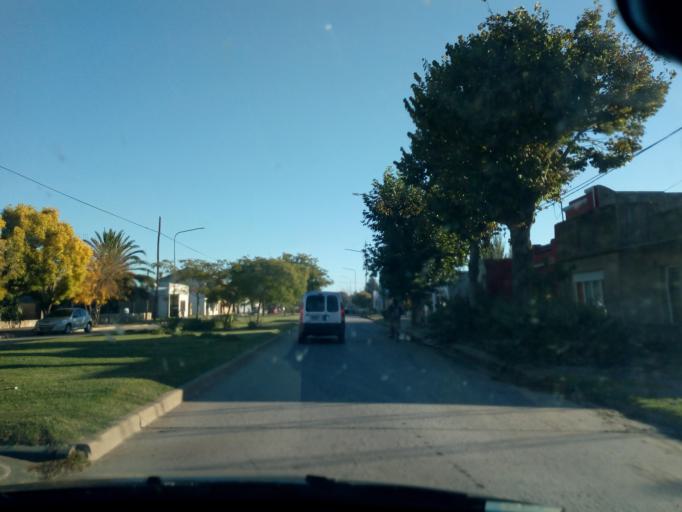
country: AR
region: Buenos Aires
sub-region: Partido de Loberia
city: Loberia
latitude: -38.1574
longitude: -58.7756
